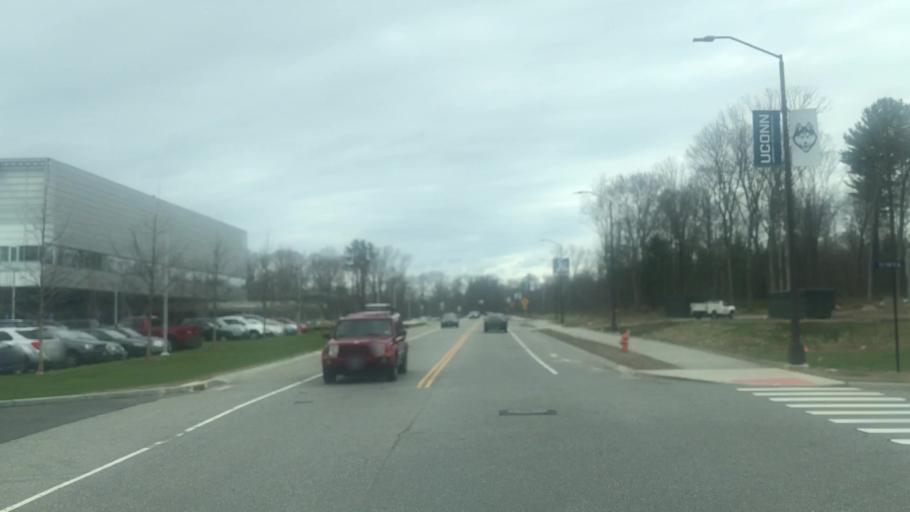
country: US
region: Connecticut
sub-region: Tolland County
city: Storrs
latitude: 41.8172
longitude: -72.2656
